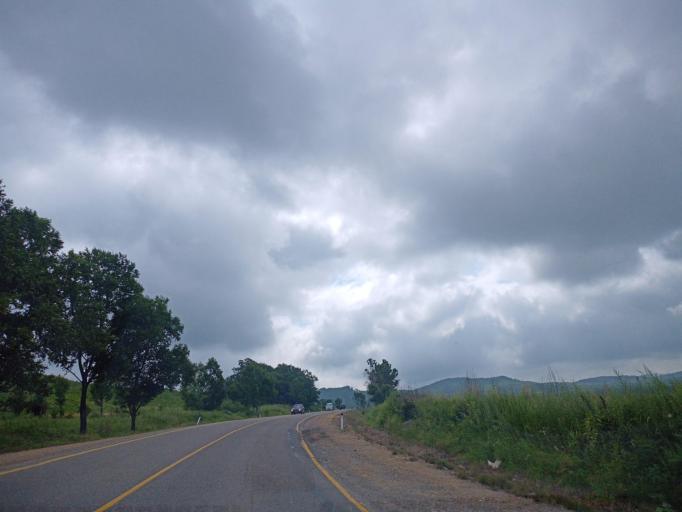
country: RU
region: Primorskiy
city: Dal'nerechensk
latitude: 46.0384
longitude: 133.8827
